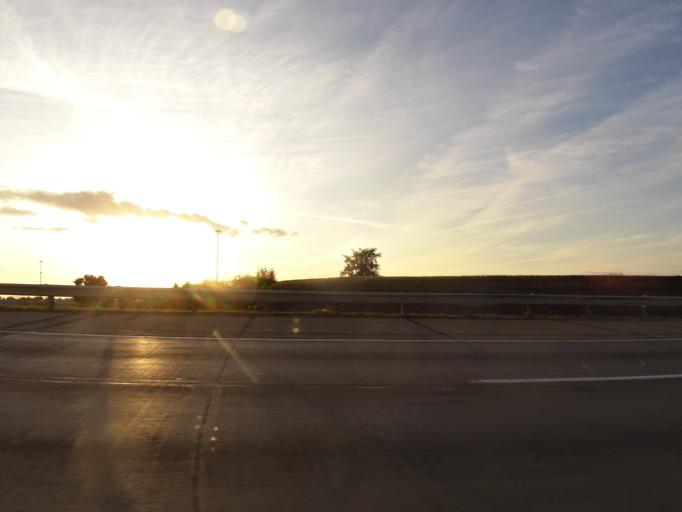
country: US
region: Indiana
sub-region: Marion County
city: Warren Park
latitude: 39.7996
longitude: -86.0346
